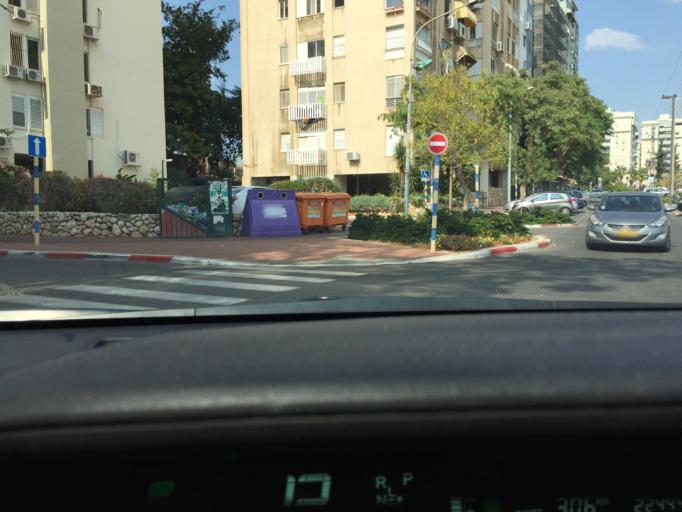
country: IL
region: Tel Aviv
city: Giv`at Shemu'el
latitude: 32.0676
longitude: 34.8468
